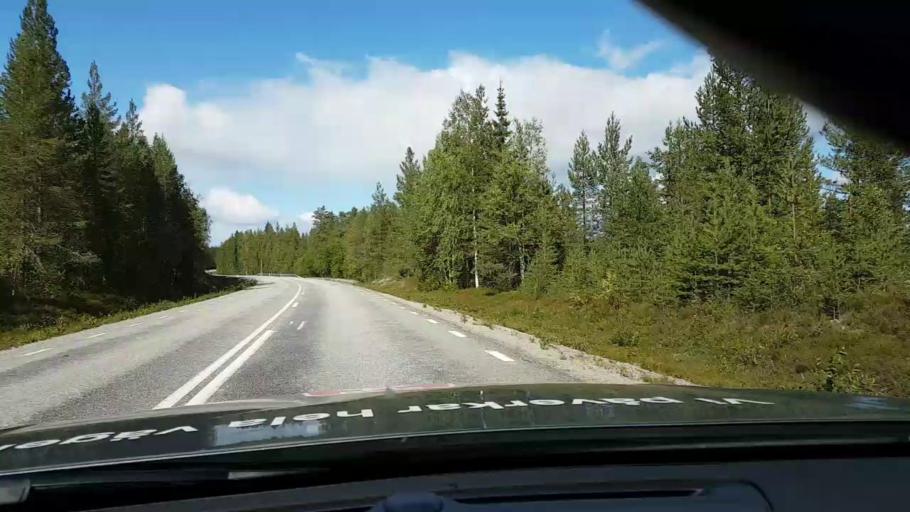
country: SE
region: Vaesternorrland
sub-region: OErnskoeldsviks Kommun
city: Bredbyn
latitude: 63.6326
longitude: 17.9098
